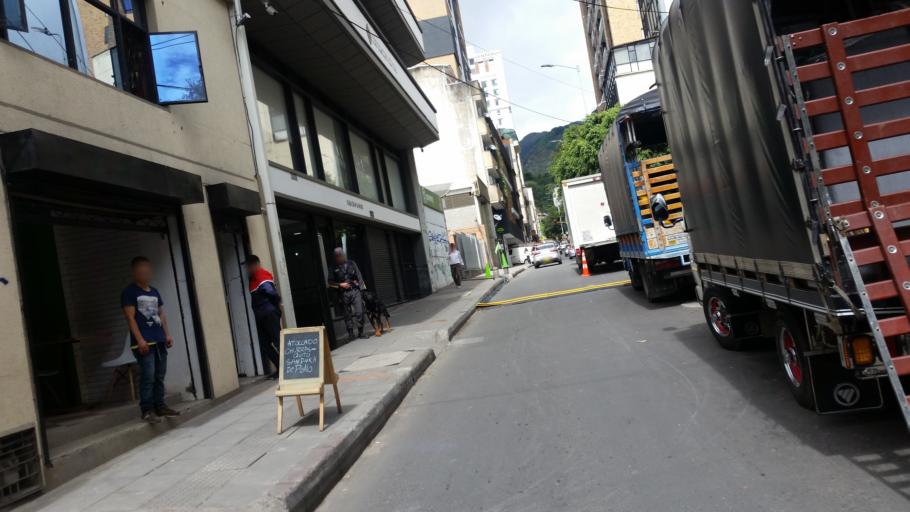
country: CO
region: Bogota D.C.
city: Bogota
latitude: 4.6088
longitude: -74.0699
